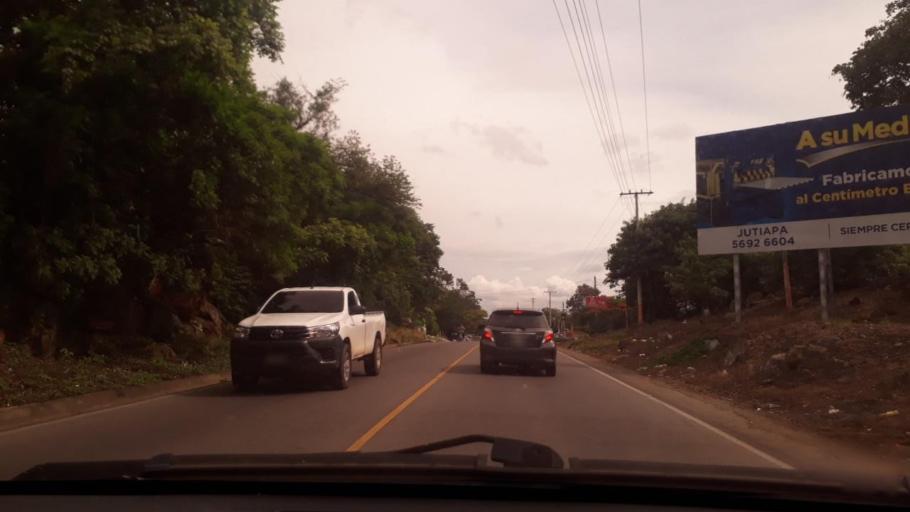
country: GT
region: Jutiapa
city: El Progreso
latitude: 14.3309
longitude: -89.8582
